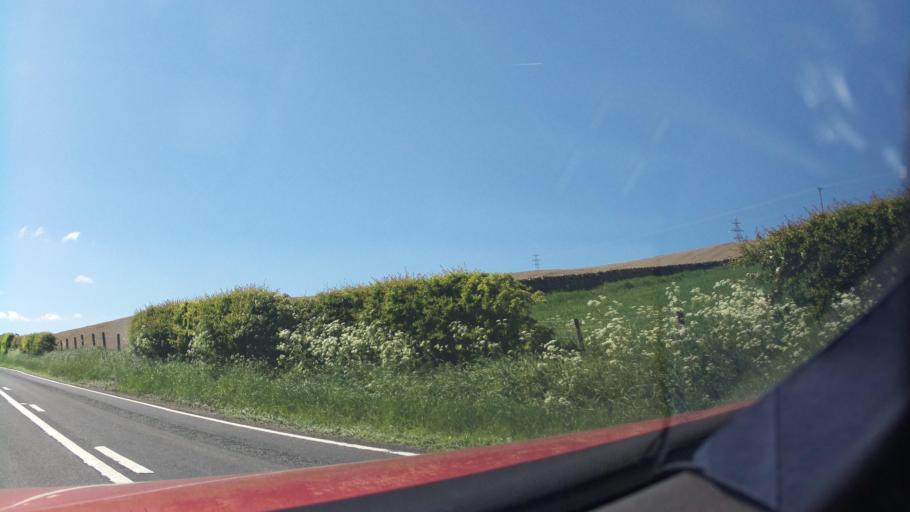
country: GB
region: Scotland
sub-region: The Scottish Borders
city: Hawick
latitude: 55.3733
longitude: -2.8770
